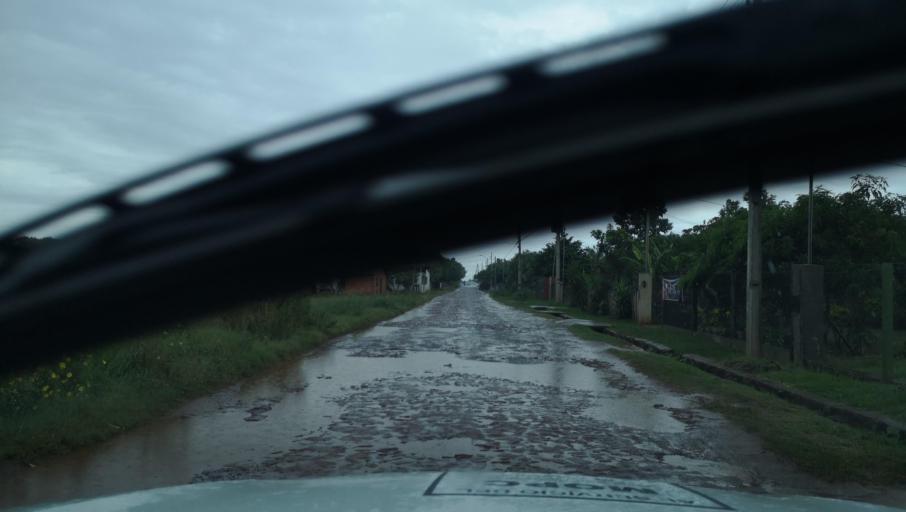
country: PY
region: Misiones
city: Santa Maria
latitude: -26.8973
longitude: -57.0349
